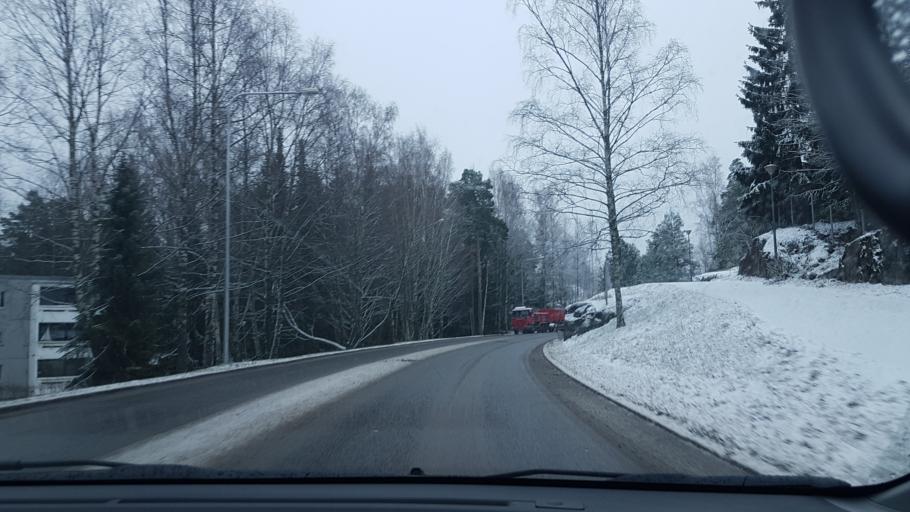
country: FI
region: Uusimaa
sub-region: Helsinki
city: Vantaa
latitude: 60.2348
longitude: 25.1284
